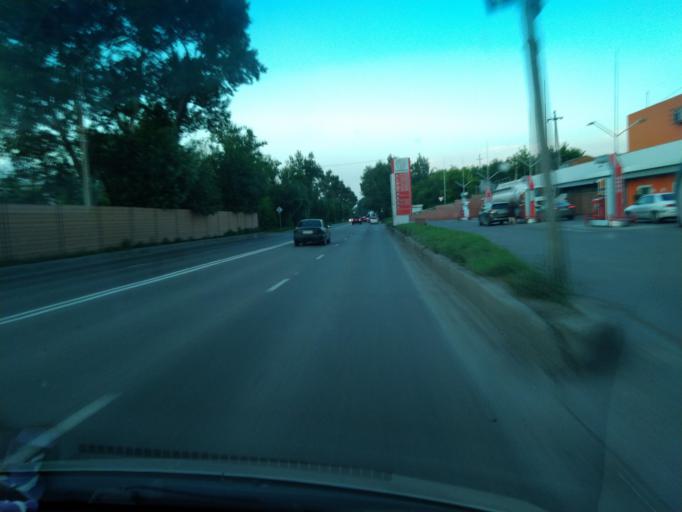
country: RU
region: Krasnoyarskiy
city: Krasnoyarsk
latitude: 55.9854
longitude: 92.8909
